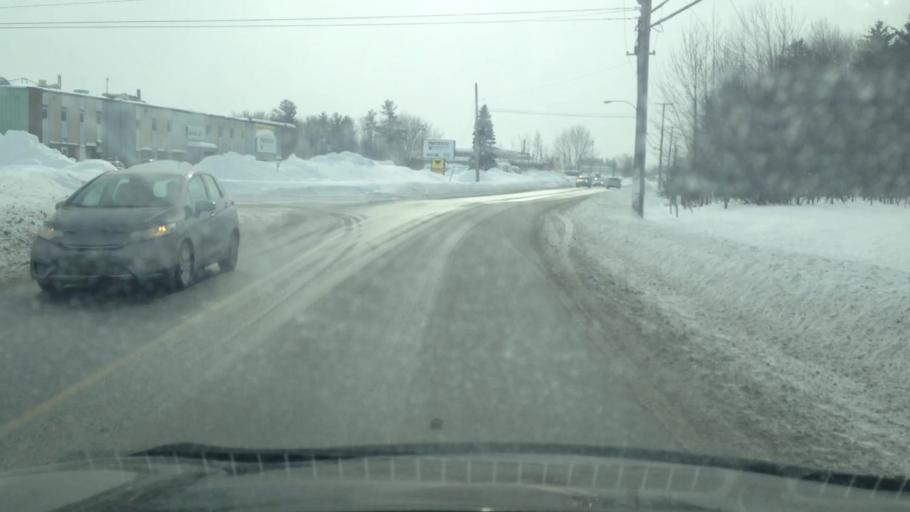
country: CA
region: Quebec
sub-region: Laurentides
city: Saint-Jerome
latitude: 45.7924
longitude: -74.0284
